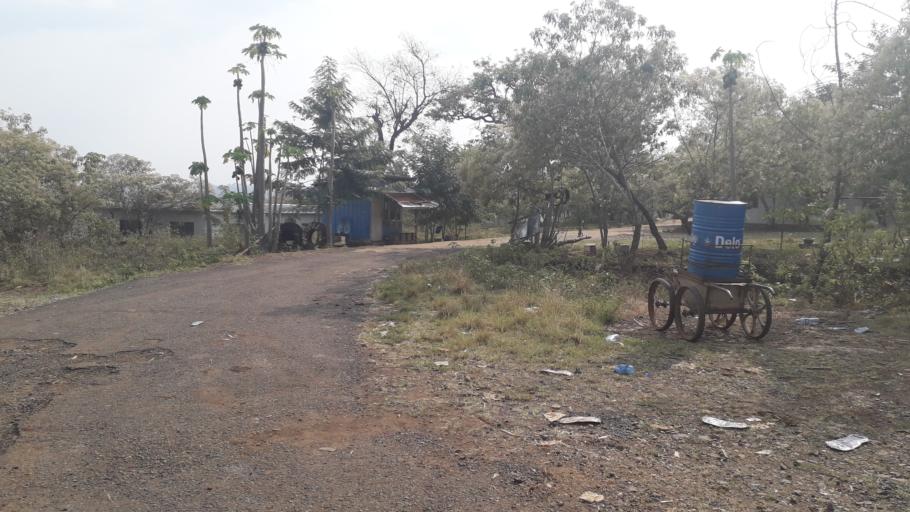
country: ET
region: Southern Nations, Nationalities, and People's Region
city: Mizan Teferi
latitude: 6.8244
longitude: 35.2895
